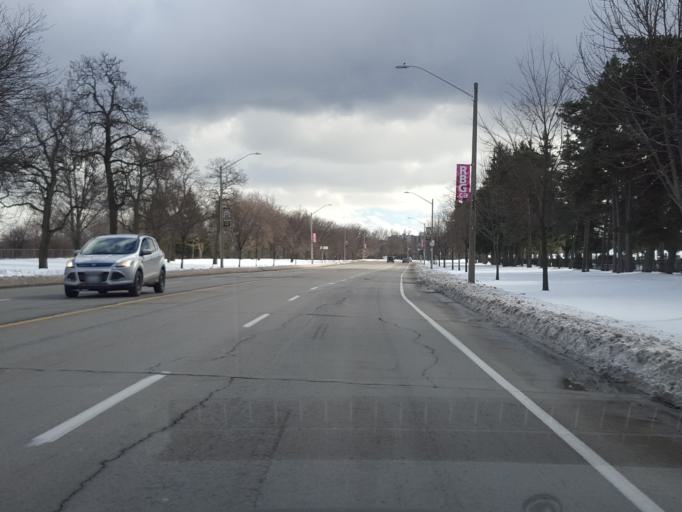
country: CA
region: Ontario
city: Hamilton
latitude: 43.2747
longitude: -79.8883
